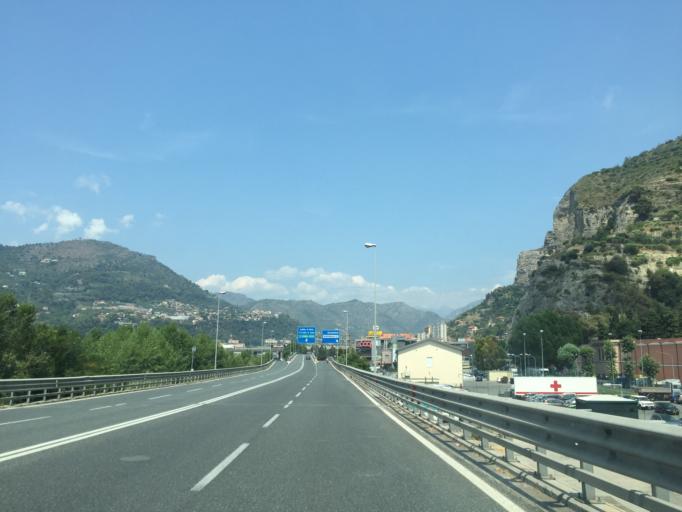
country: IT
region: Liguria
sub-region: Provincia di Imperia
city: Ventimiglia
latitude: 43.7973
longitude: 7.6013
